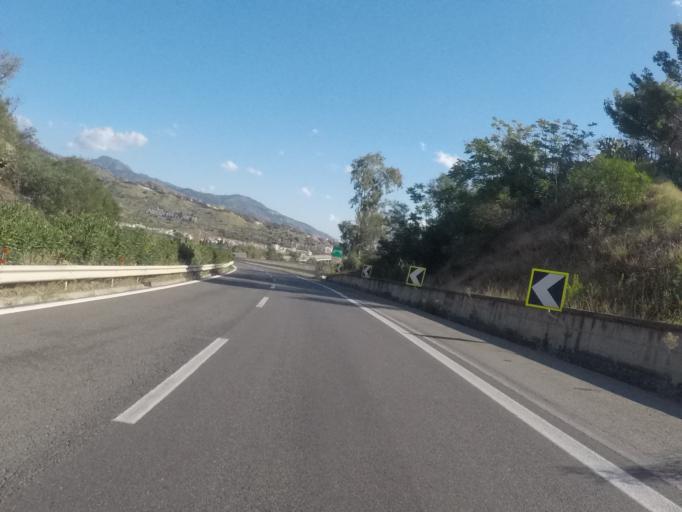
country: IT
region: Sicily
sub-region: Messina
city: Santa Teresa di Riva
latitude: 37.9524
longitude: 15.3690
